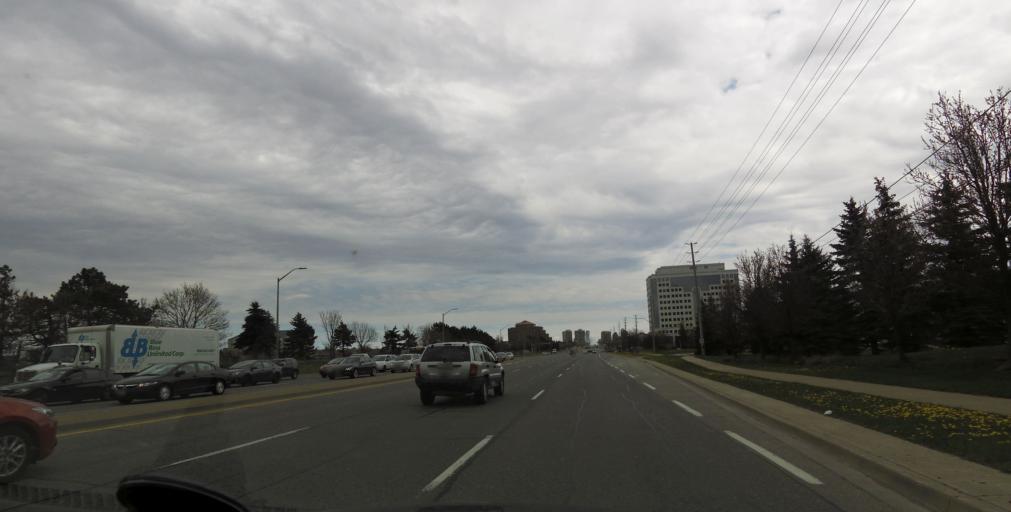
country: CA
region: Ontario
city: Mississauga
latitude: 43.6246
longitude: -79.6775
